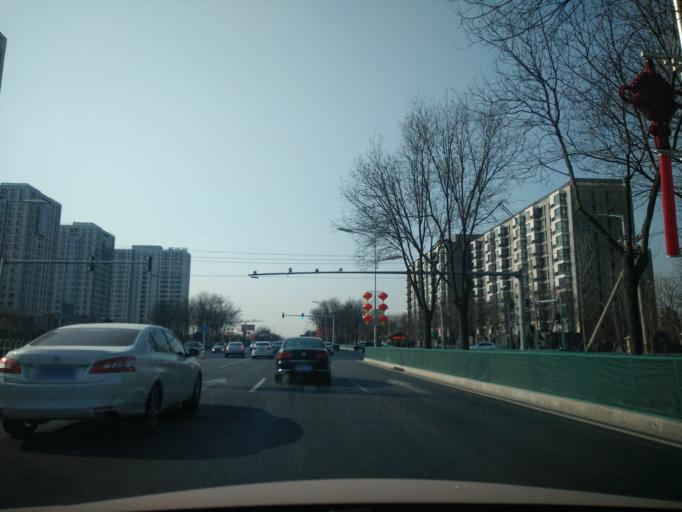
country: CN
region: Beijing
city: Jiugong
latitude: 39.7859
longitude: 116.4919
